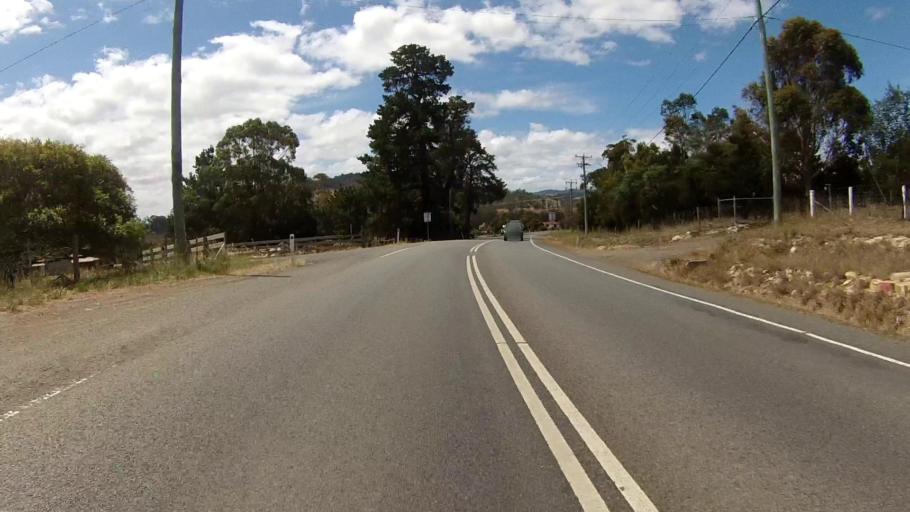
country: AU
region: Tasmania
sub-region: Sorell
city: Sorell
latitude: -42.8067
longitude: 147.6290
